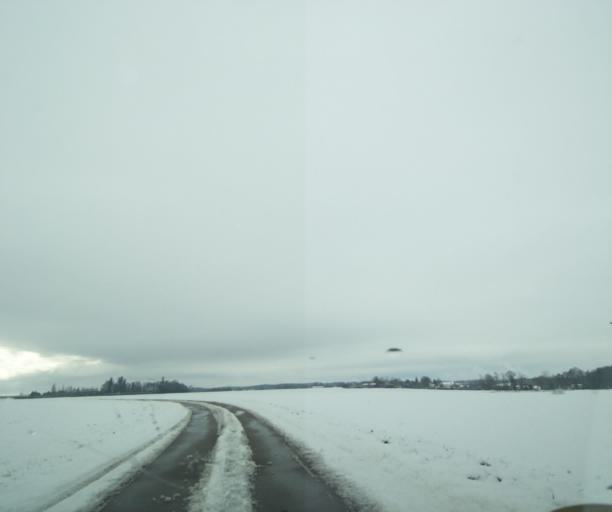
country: FR
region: Champagne-Ardenne
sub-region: Departement de la Haute-Marne
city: Montier-en-Der
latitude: 48.4626
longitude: 4.6503
